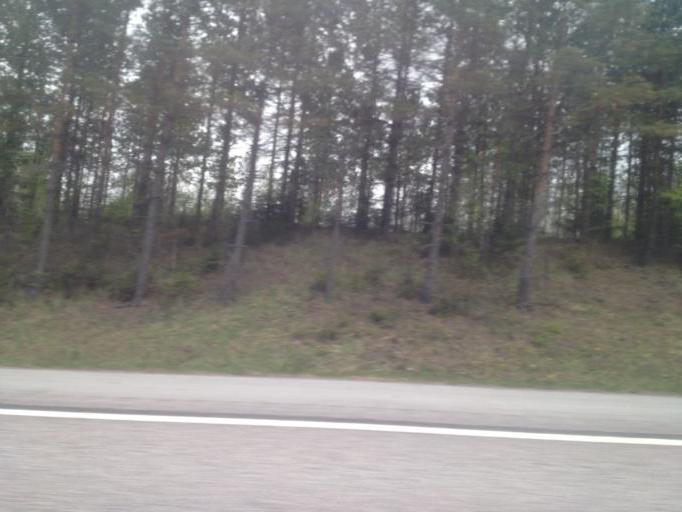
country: FI
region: Uusimaa
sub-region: Helsinki
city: Hyvinge
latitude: 60.6435
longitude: 24.8080
